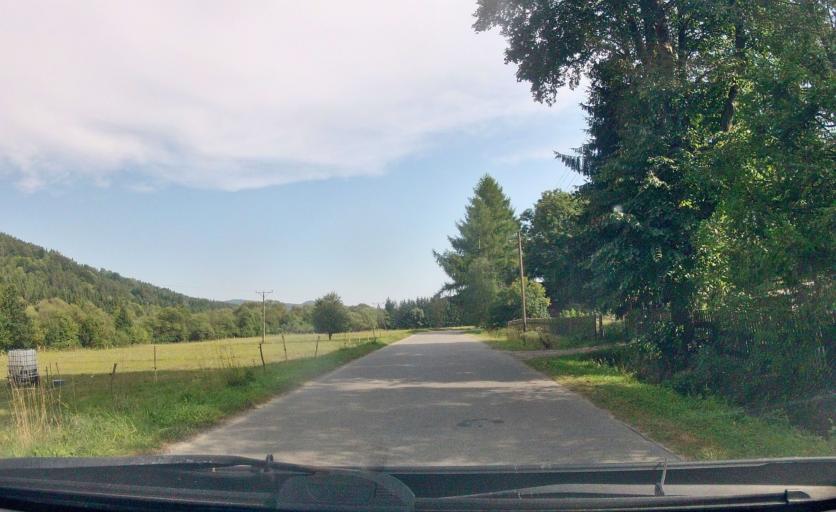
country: PL
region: Subcarpathian Voivodeship
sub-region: Powiat jasielski
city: Krempna
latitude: 49.5044
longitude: 21.5395
